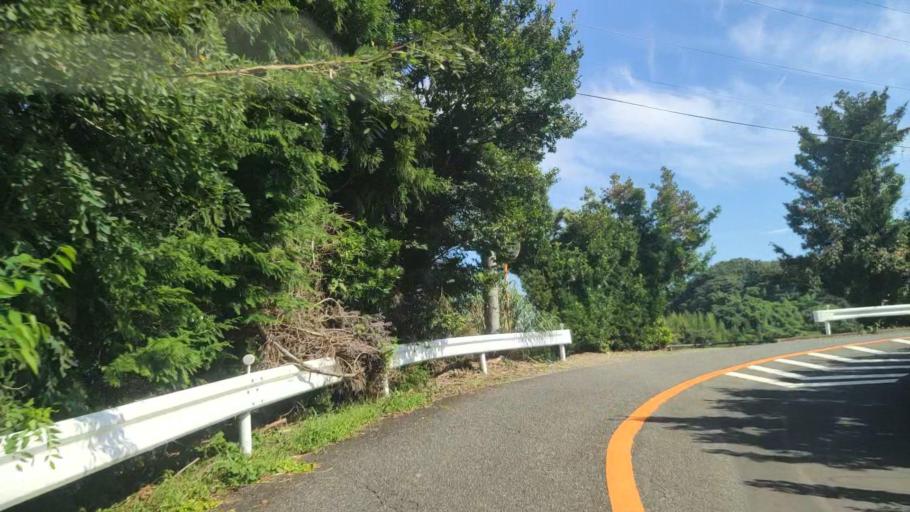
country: JP
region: Shizuoka
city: Shizuoka-shi
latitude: 34.9832
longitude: 138.4788
